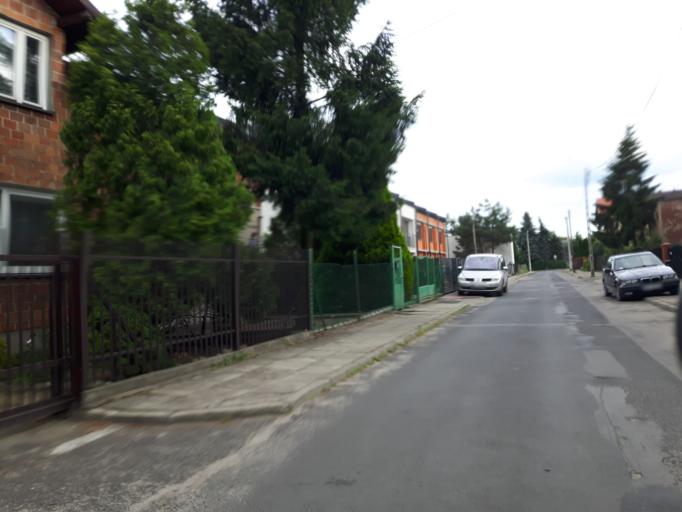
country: PL
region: Masovian Voivodeship
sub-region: Powiat wolominski
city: Zabki
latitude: 52.2850
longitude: 21.1160
